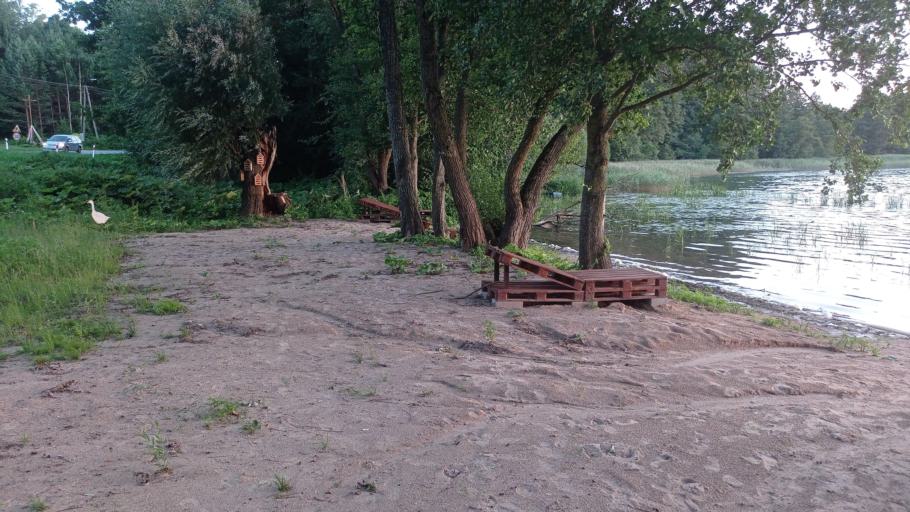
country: PL
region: Warmian-Masurian Voivodeship
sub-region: Powiat olecki
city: Olecko
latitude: 53.9397
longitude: 22.4373
